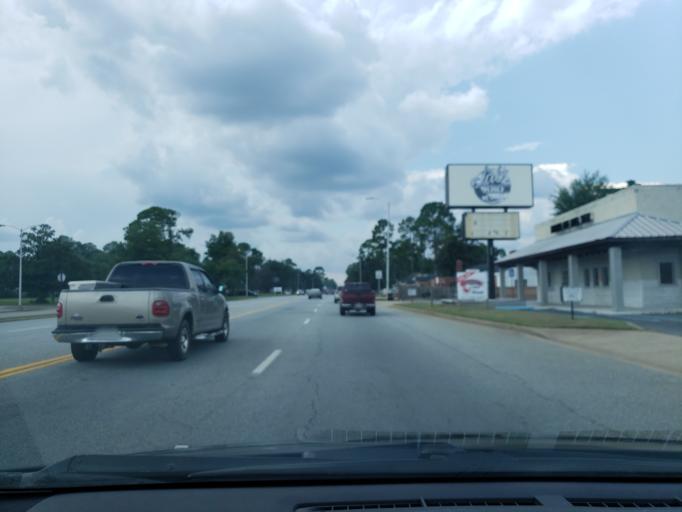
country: US
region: Georgia
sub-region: Dougherty County
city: Albany
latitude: 31.5820
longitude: -84.1768
